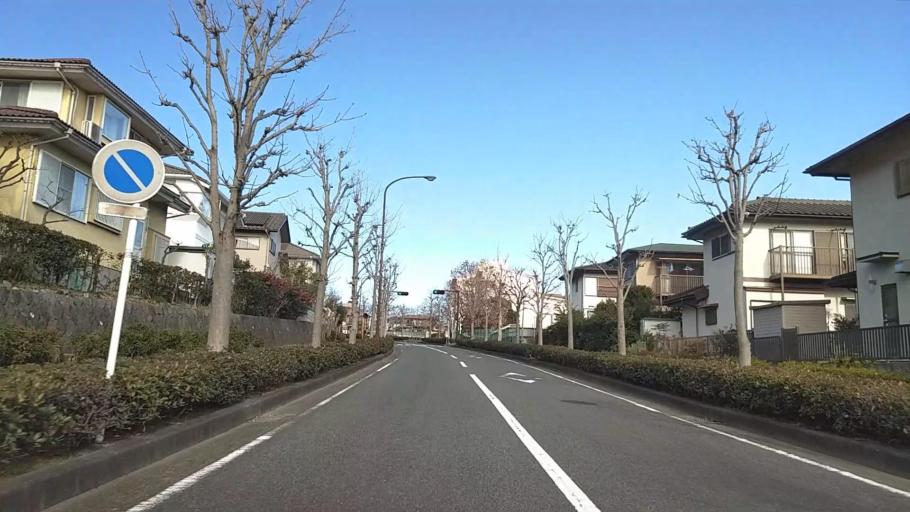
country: JP
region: Kanagawa
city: Isehara
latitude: 35.4433
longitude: 139.3059
